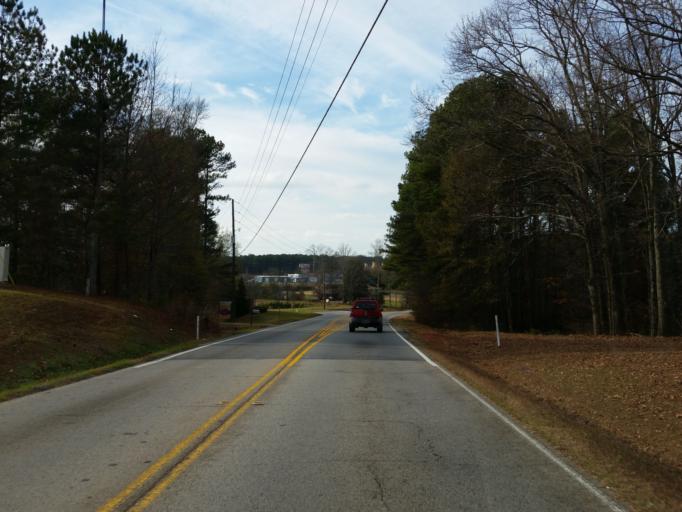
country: US
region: Georgia
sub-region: Paulding County
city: Hiram
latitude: 33.9139
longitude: -84.7656
